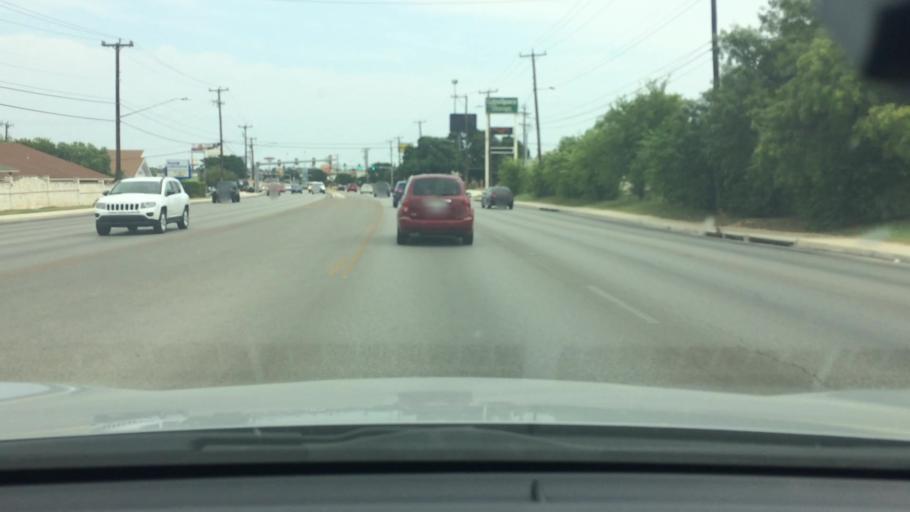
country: US
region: Texas
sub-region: Bexar County
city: Leon Valley
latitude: 29.4709
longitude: -98.6514
